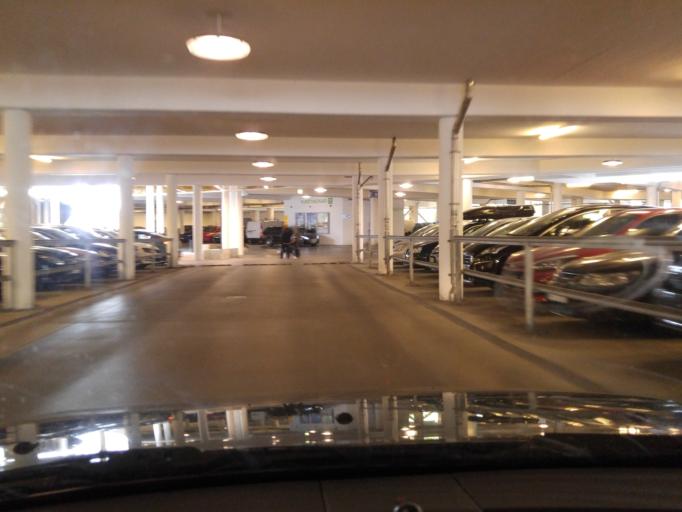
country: SE
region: Vaestra Goetaland
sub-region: Goteborg
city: Majorna
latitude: 57.6531
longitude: 11.9142
